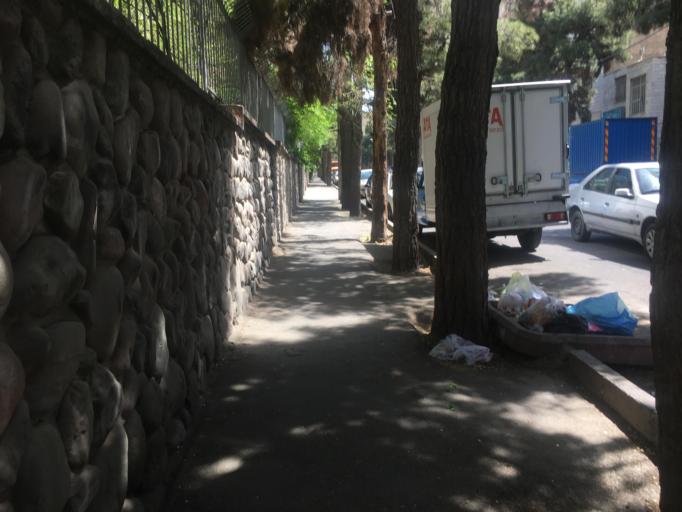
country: IR
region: Tehran
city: Tehran
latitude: 35.7434
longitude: 51.5460
